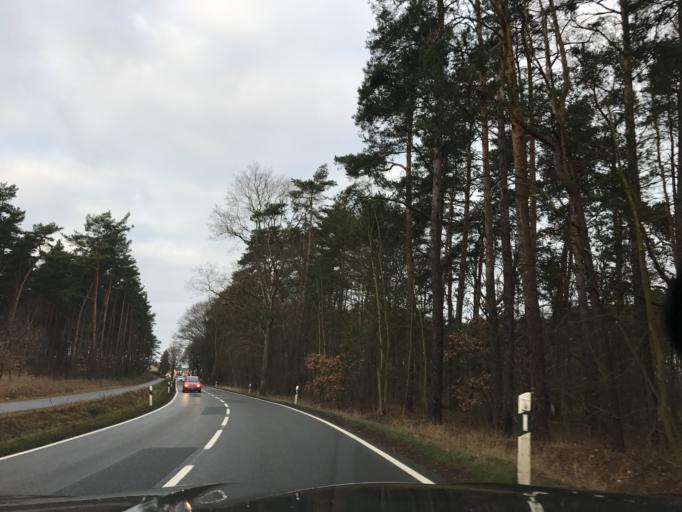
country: DE
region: Brandenburg
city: Golzow
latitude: 52.3457
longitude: 12.6387
